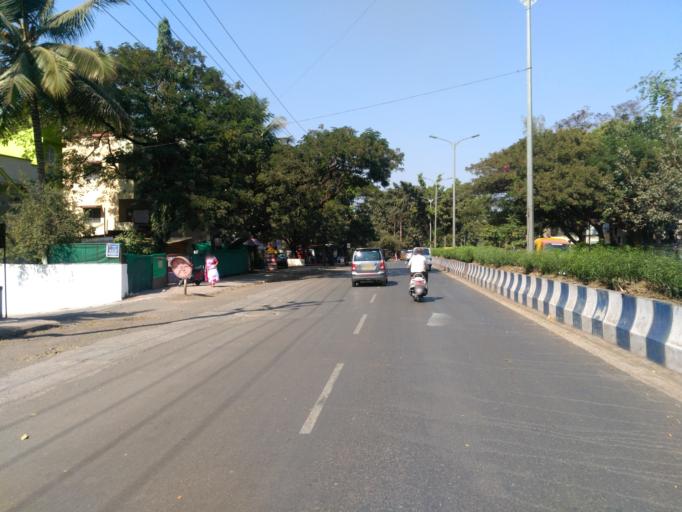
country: IN
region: Maharashtra
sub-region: Pune Division
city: Pune
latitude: 18.4738
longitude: 73.8626
